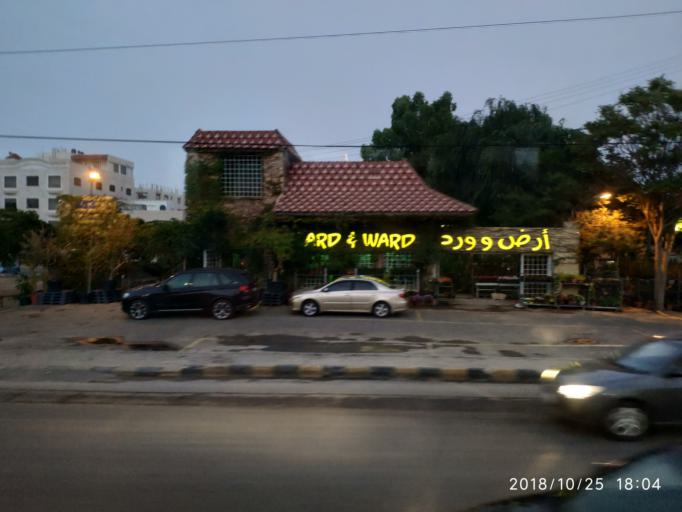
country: JO
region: Amman
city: Wadi as Sir
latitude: 31.9709
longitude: 35.8405
